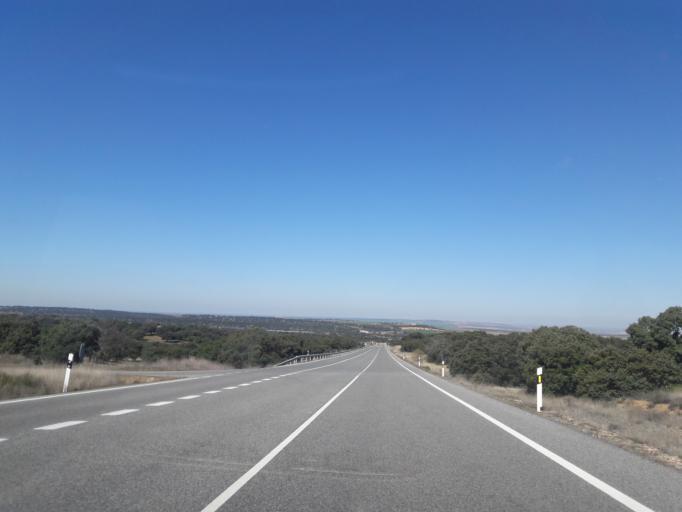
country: ES
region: Castille and Leon
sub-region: Provincia de Salamanca
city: Martinamor
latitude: 40.8175
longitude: -5.6307
